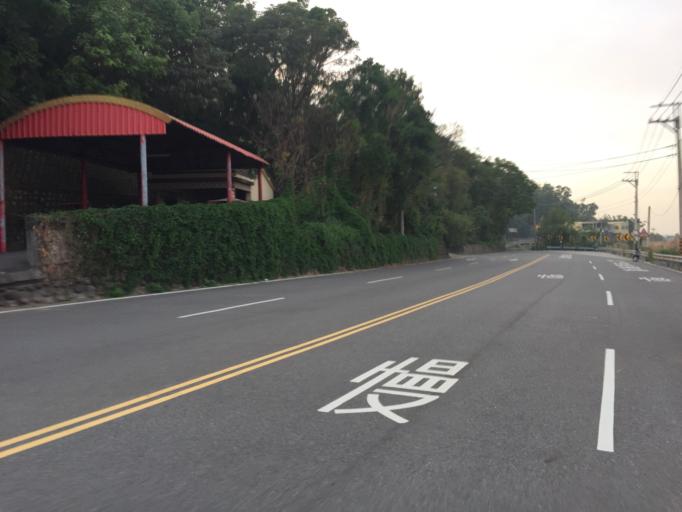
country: TW
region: Taiwan
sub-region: Miaoli
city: Miaoli
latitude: 24.4780
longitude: 120.7772
